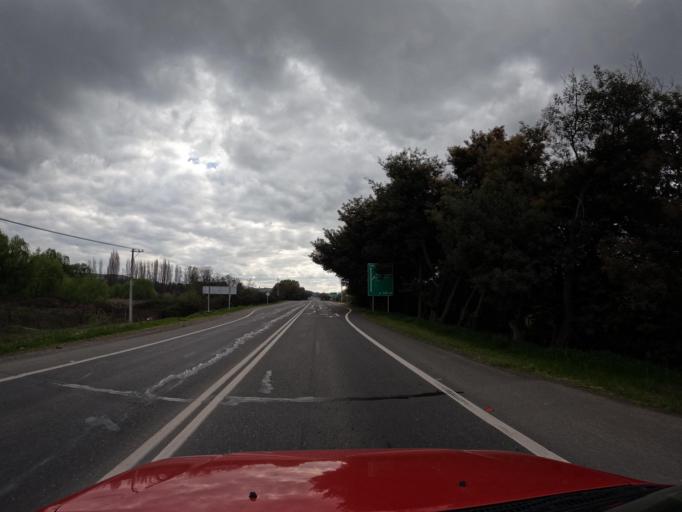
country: CL
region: Maule
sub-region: Provincia de Linares
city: San Javier
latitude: -35.6266
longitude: -71.7428
